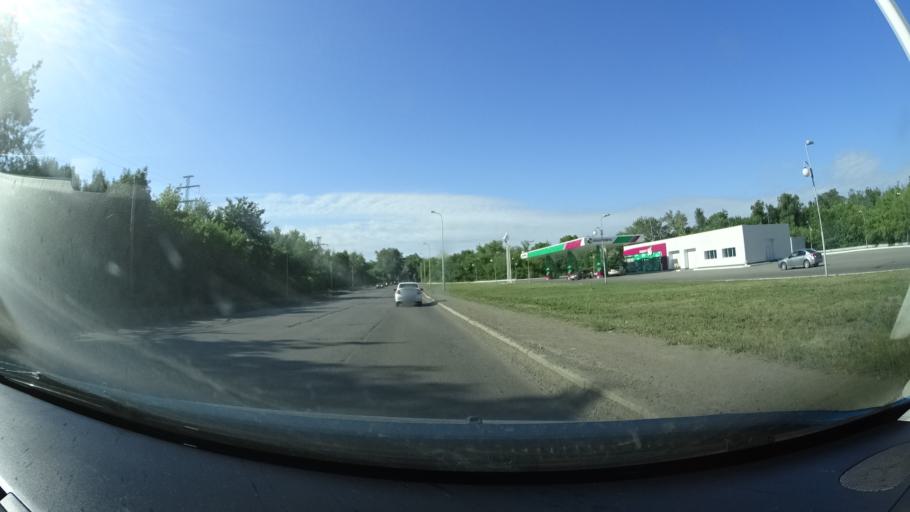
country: RU
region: Bashkortostan
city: Ufa
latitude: 54.8469
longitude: 56.0765
